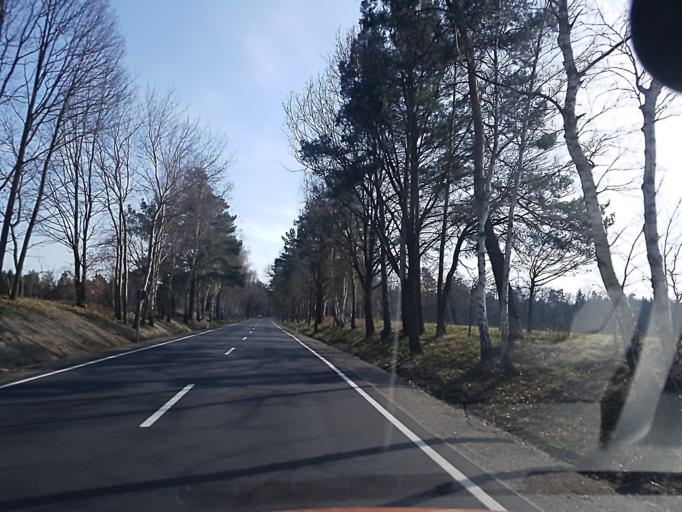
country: DE
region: Brandenburg
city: Bronkow
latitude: 51.7021
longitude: 13.9193
